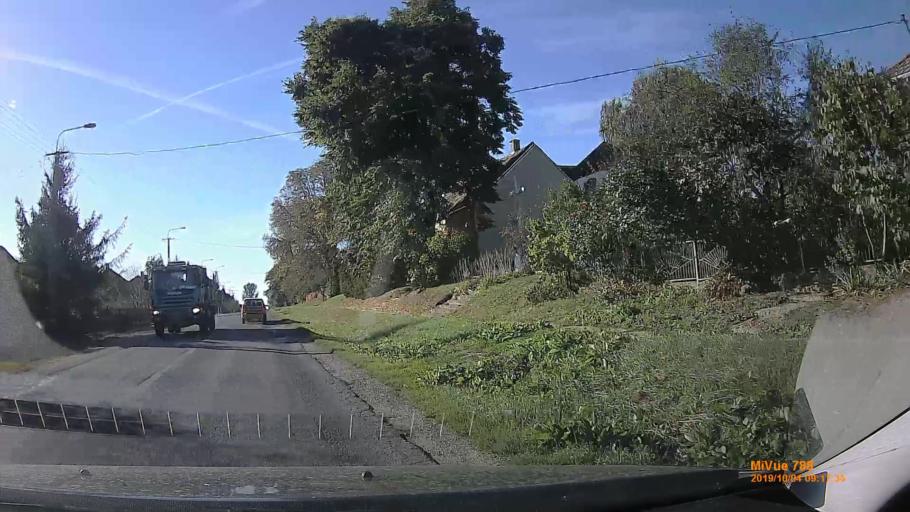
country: HU
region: Somogy
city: Karad
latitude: 46.6010
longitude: 17.8002
